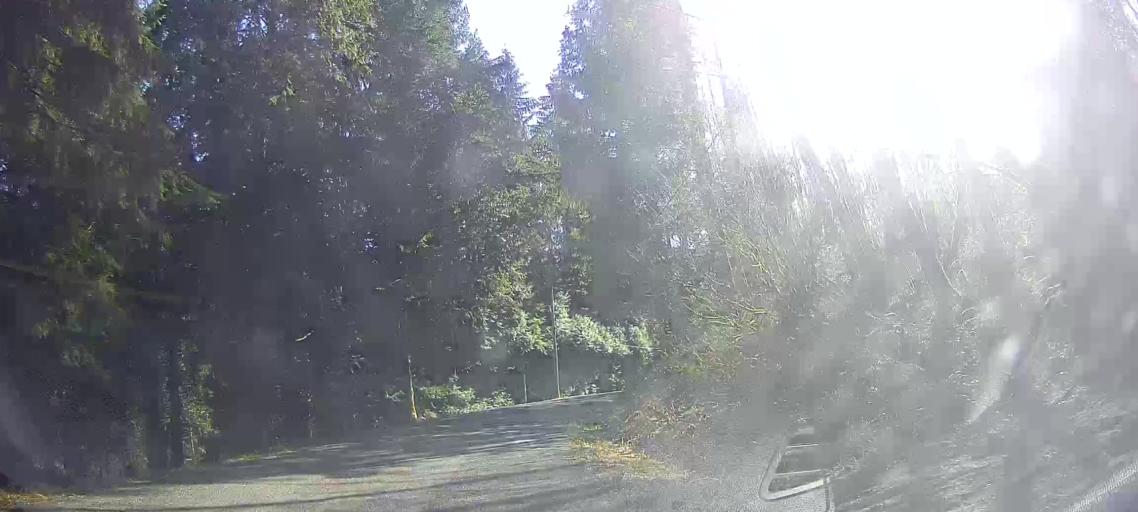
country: US
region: Washington
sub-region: Whatcom County
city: Sudden Valley
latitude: 48.6154
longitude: -122.3671
